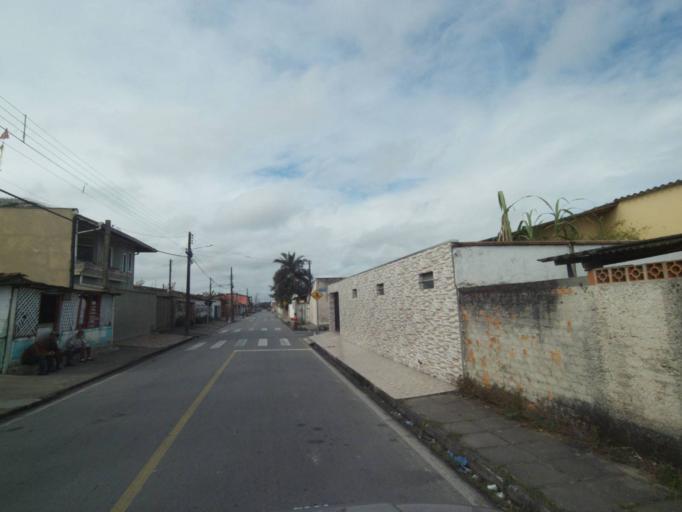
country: BR
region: Parana
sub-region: Paranagua
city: Paranagua
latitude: -25.5651
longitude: -48.5626
